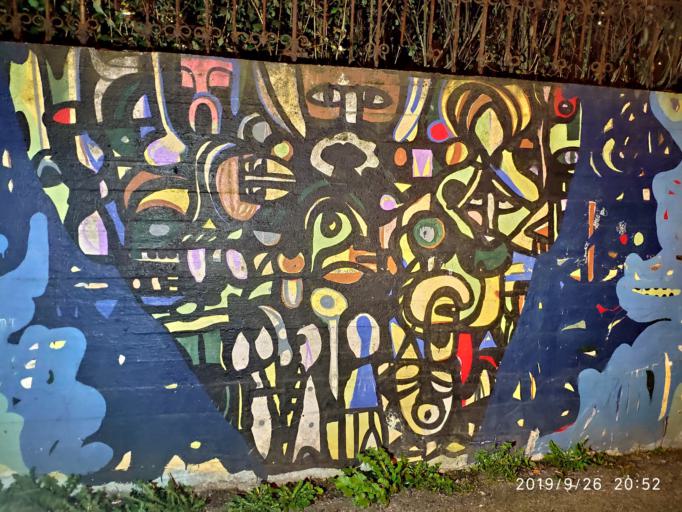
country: NO
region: Rogaland
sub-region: Haugesund
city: Haugesund
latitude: 59.4138
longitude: 5.2694
